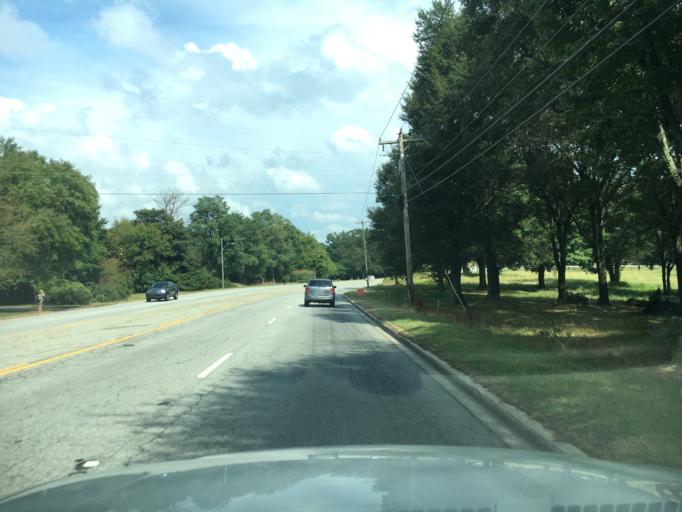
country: US
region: South Carolina
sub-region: Greenville County
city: Wade Hampton
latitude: 34.8587
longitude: -82.3312
